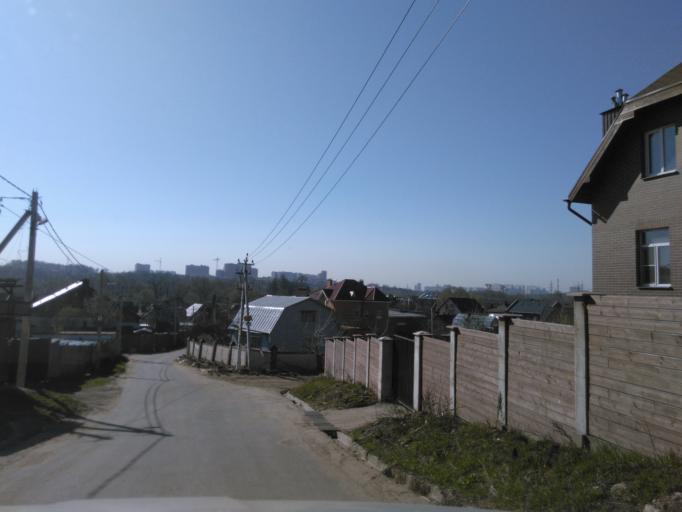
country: RU
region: Moscow
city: Khimki
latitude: 55.8789
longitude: 37.3743
